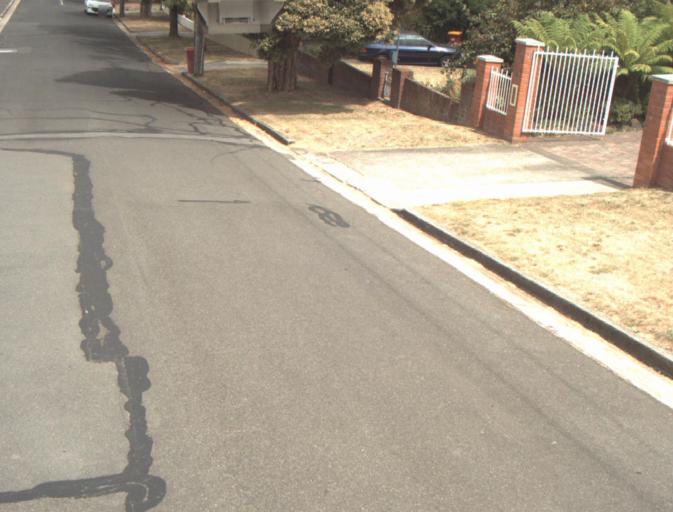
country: AU
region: Tasmania
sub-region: Launceston
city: East Launceston
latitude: -41.4490
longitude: 147.1494
